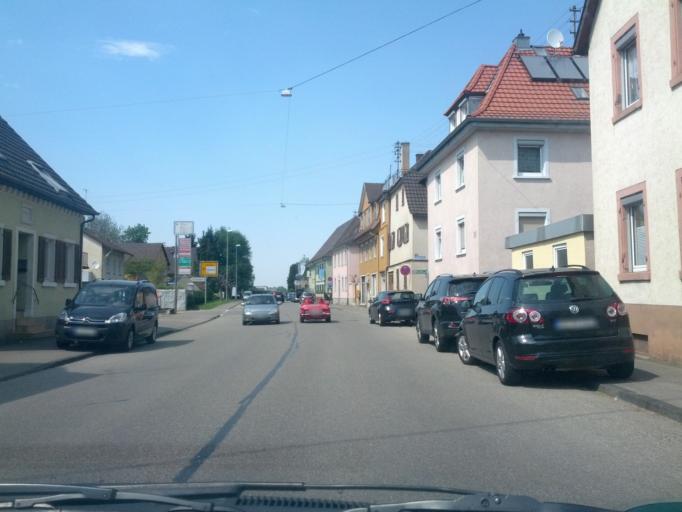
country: DE
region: Baden-Wuerttemberg
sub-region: Freiburg Region
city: Herbolzheim
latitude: 48.2235
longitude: 7.7778
